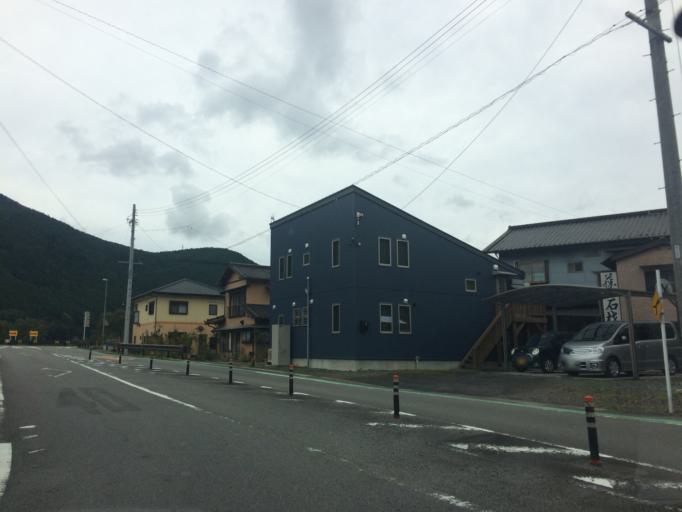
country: JP
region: Shizuoka
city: Kanaya
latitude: 35.0404
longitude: 138.0813
